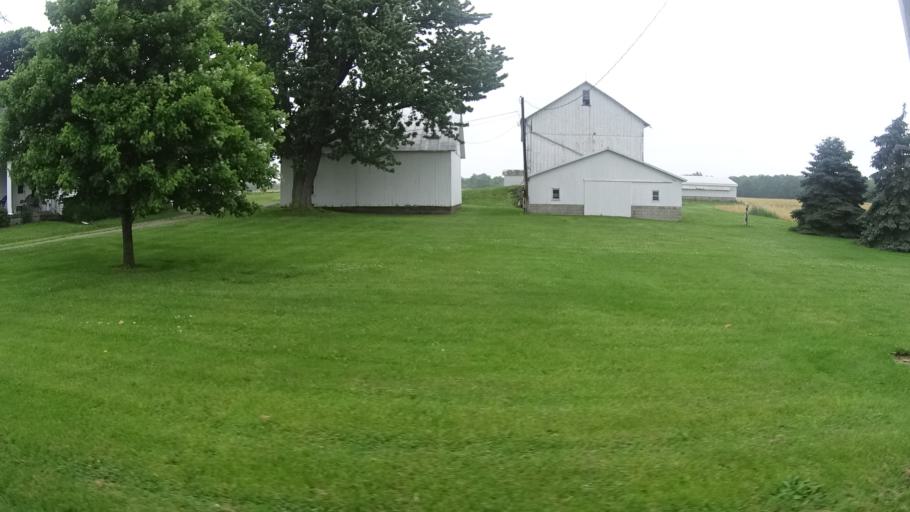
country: US
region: Ohio
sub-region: Huron County
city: Bellevue
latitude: 41.3587
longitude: -82.8293
